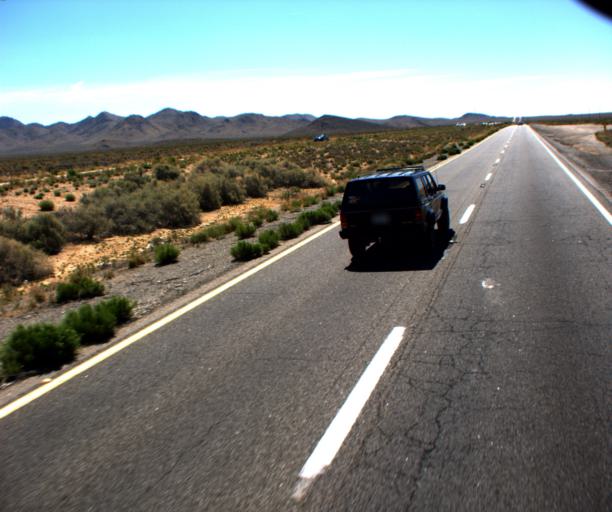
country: US
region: Arizona
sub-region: Mohave County
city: Dolan Springs
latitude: 35.4787
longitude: -114.3174
